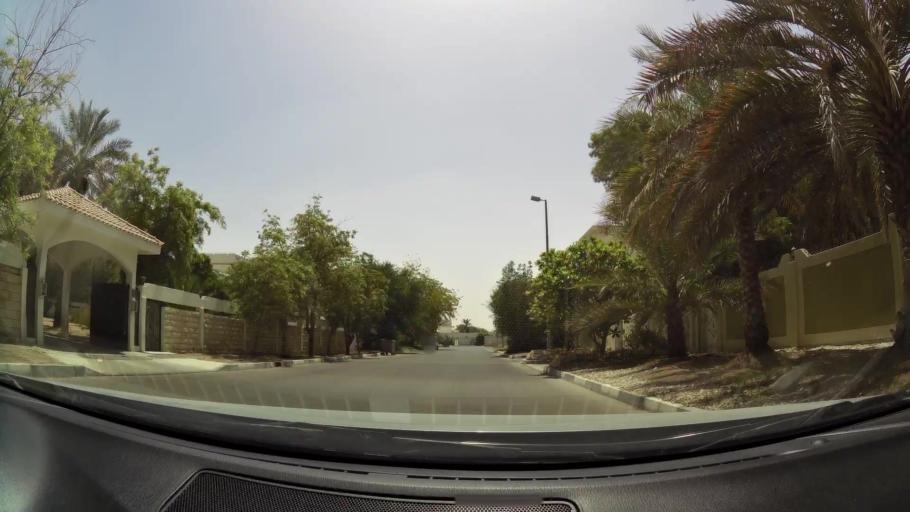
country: AE
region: Abu Dhabi
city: Al Ain
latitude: 24.2360
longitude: 55.7154
